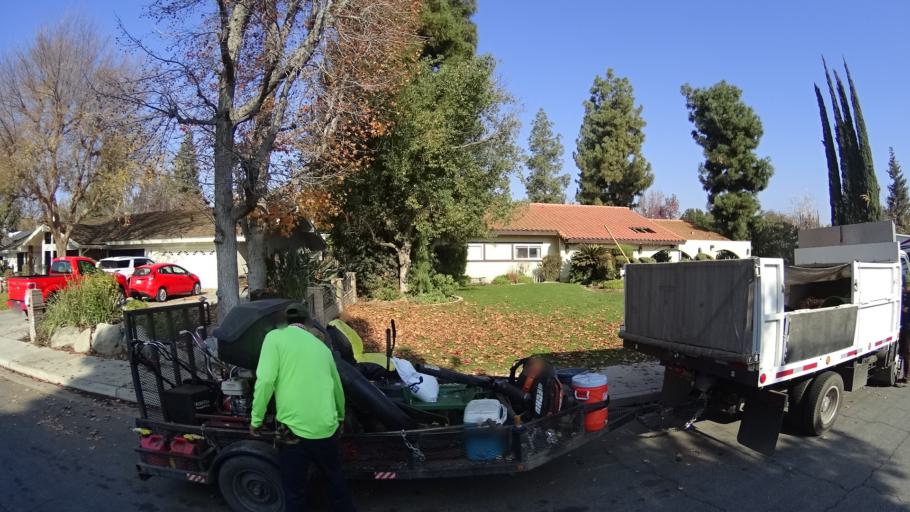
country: US
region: California
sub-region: Kern County
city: Greenacres
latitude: 35.3592
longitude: -119.0782
